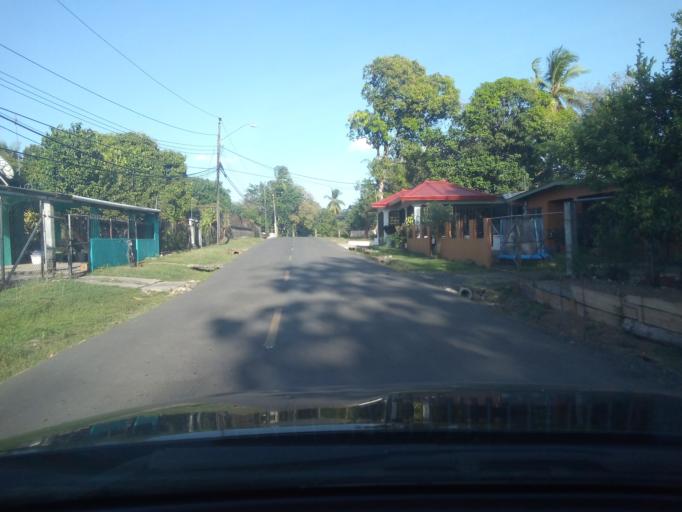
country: PA
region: Veraguas
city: Atalaya
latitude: 8.0395
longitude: -80.9245
